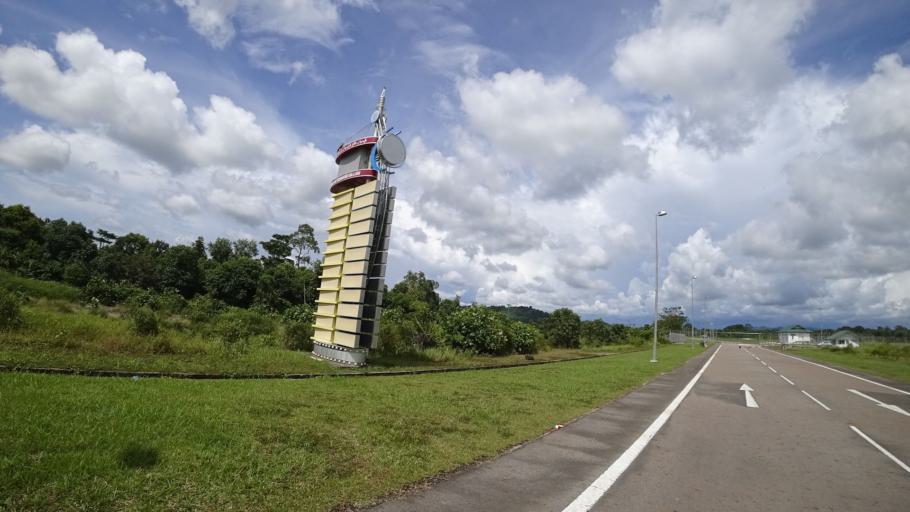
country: BN
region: Tutong
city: Tutong
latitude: 4.7490
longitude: 114.8192
